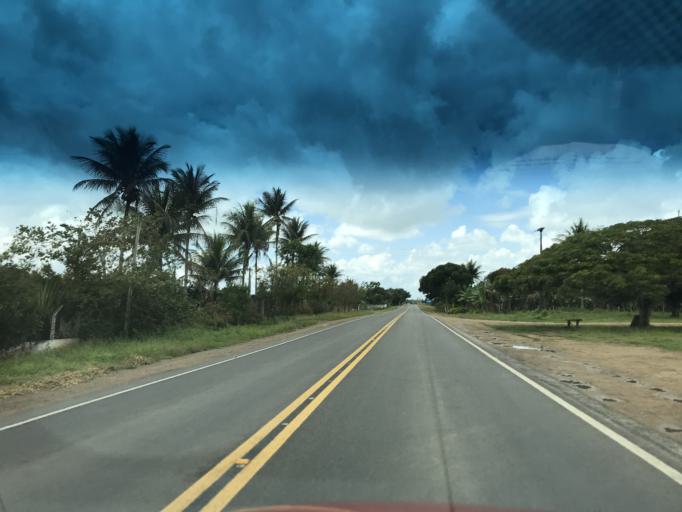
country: BR
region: Bahia
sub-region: Conceicao Do Almeida
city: Conceicao do Almeida
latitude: -12.7208
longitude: -39.2126
